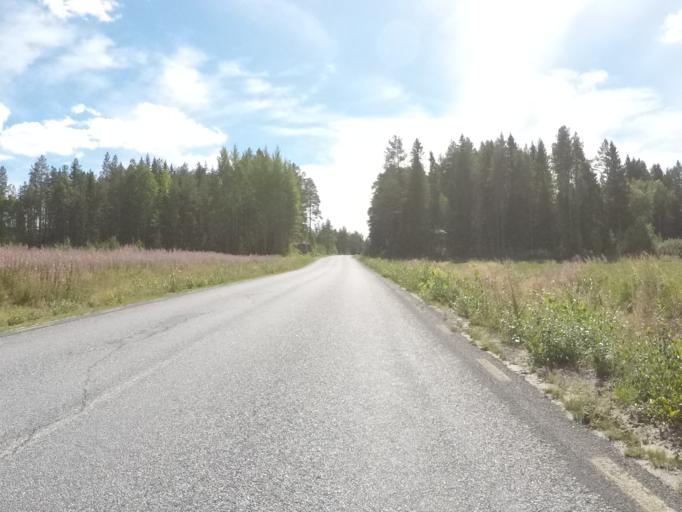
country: SE
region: Vaesterbotten
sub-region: Robertsfors Kommun
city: Robertsfors
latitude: 63.9869
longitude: 20.8118
